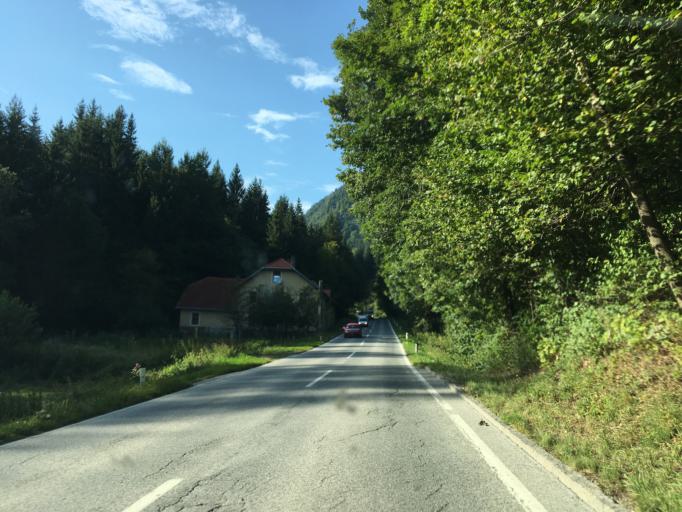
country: AT
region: Carinthia
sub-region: Politischer Bezirk Sankt Veit an der Glan
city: Bruckl
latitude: 46.7150
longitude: 14.5619
